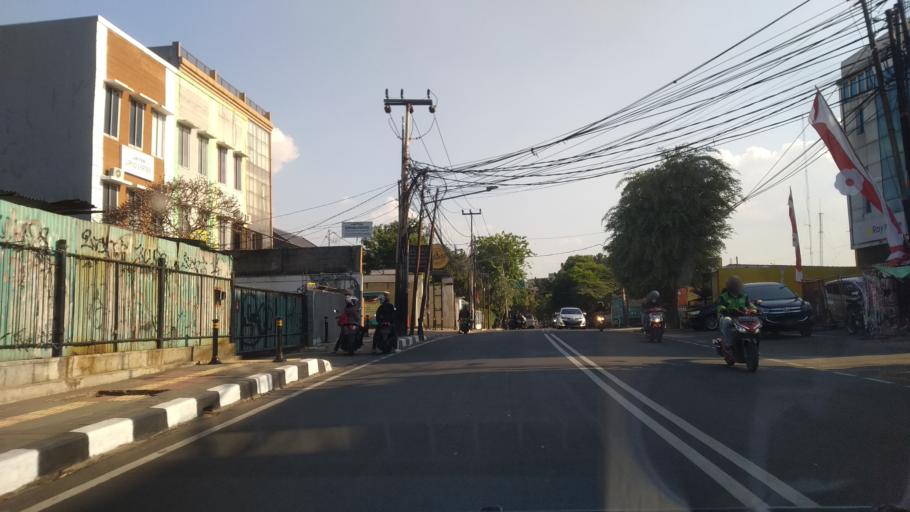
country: ID
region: Banten
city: South Tangerang
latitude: -6.2566
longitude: 106.7685
